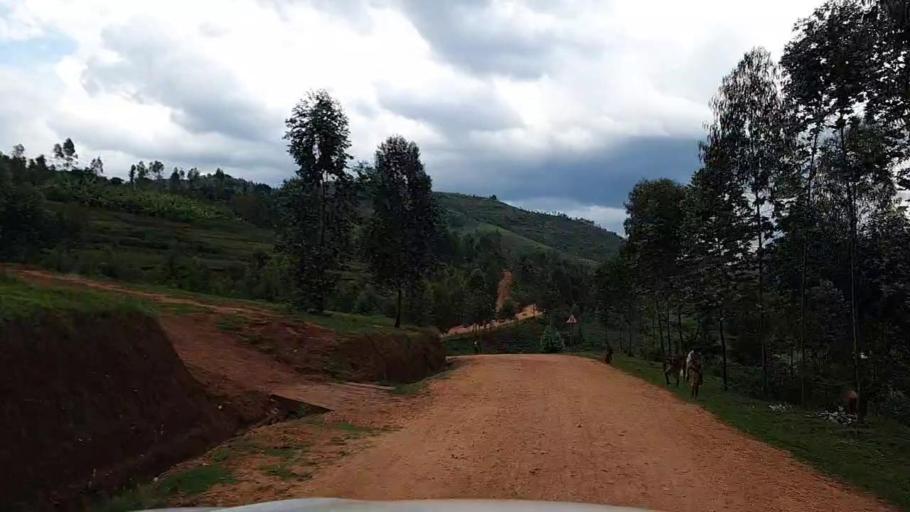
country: RW
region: Southern Province
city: Nyanza
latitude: -2.4013
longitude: 29.6772
